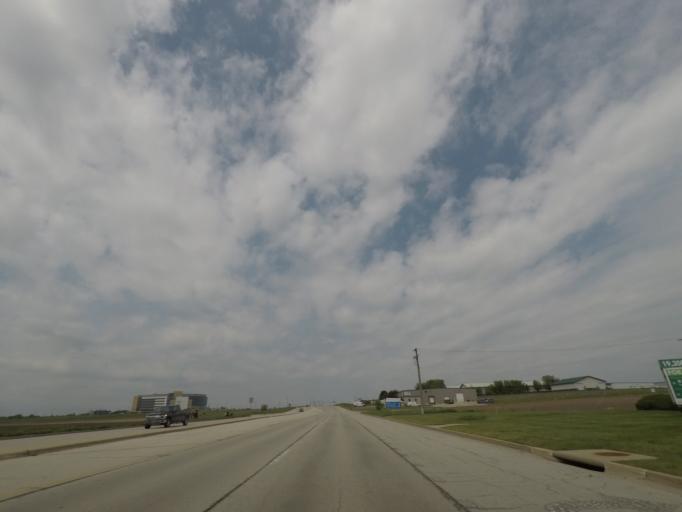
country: US
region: Illinois
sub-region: Winnebago County
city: Cherry Valley
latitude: 42.3194
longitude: -88.9514
